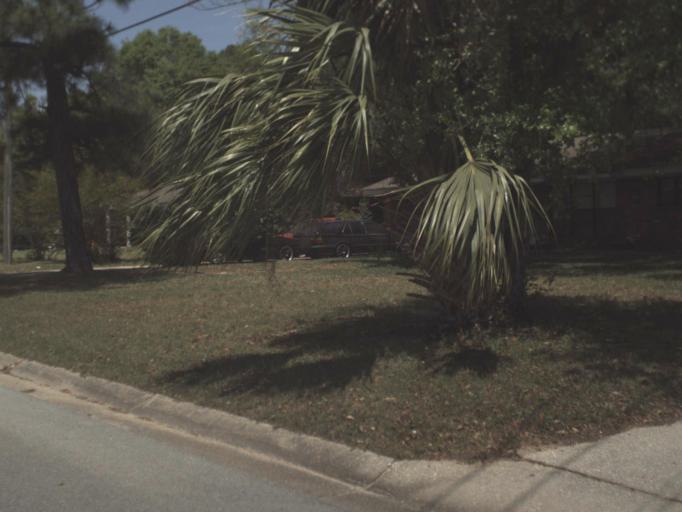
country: US
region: Florida
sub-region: Escambia County
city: Goulding
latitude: 30.4611
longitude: -87.2010
